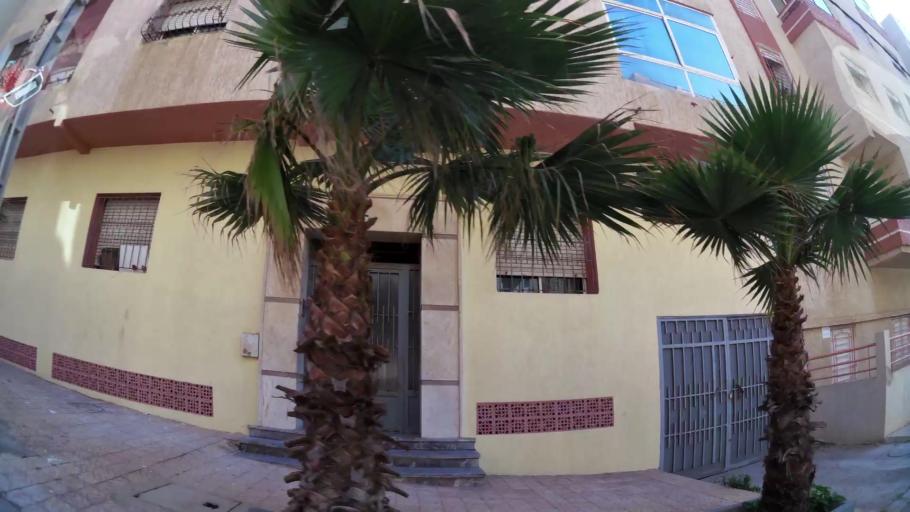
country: MA
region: Rabat-Sale-Zemmour-Zaer
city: Sale
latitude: 34.0691
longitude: -6.8024
